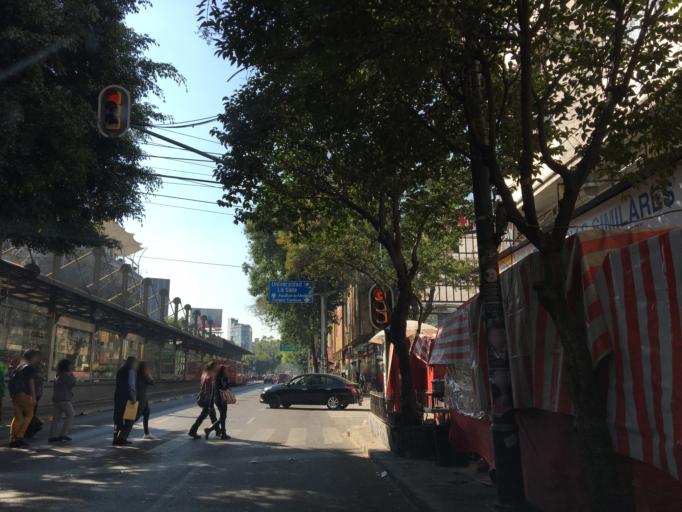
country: MX
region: Mexico City
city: Benito Juarez
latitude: 19.4072
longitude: -99.1682
